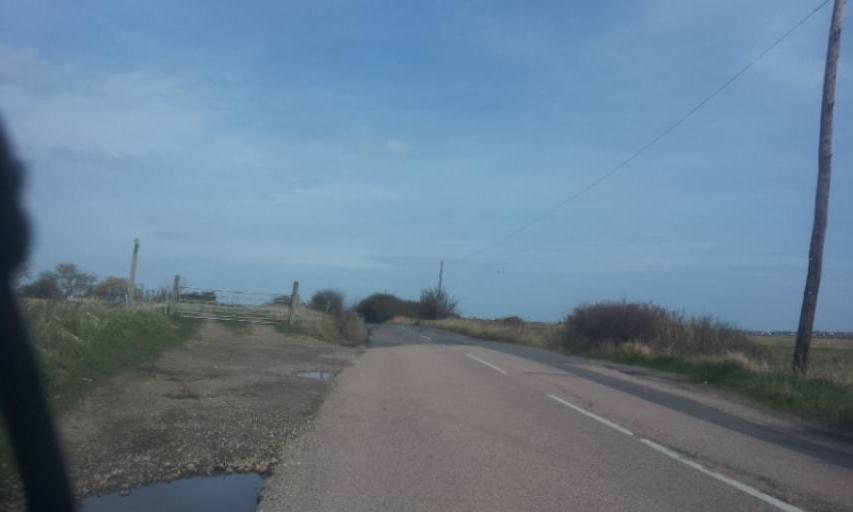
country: GB
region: England
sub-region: Kent
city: Dunkirk
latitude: 51.3414
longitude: 0.9569
